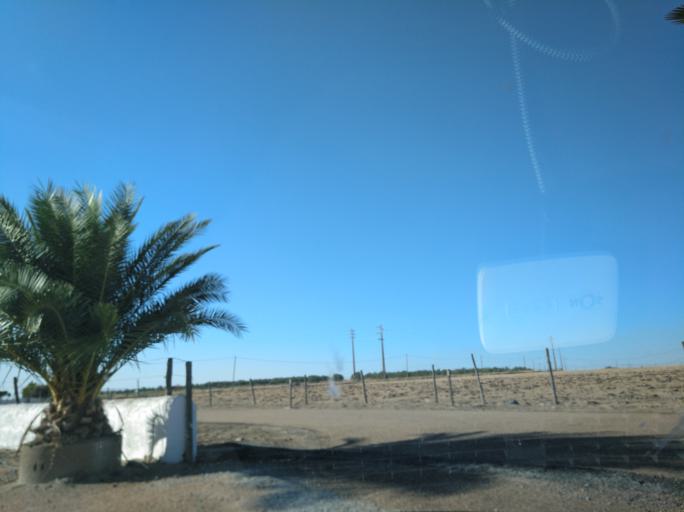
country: PT
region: Portalegre
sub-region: Elvas
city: Elvas
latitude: 38.9460
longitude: -7.1883
